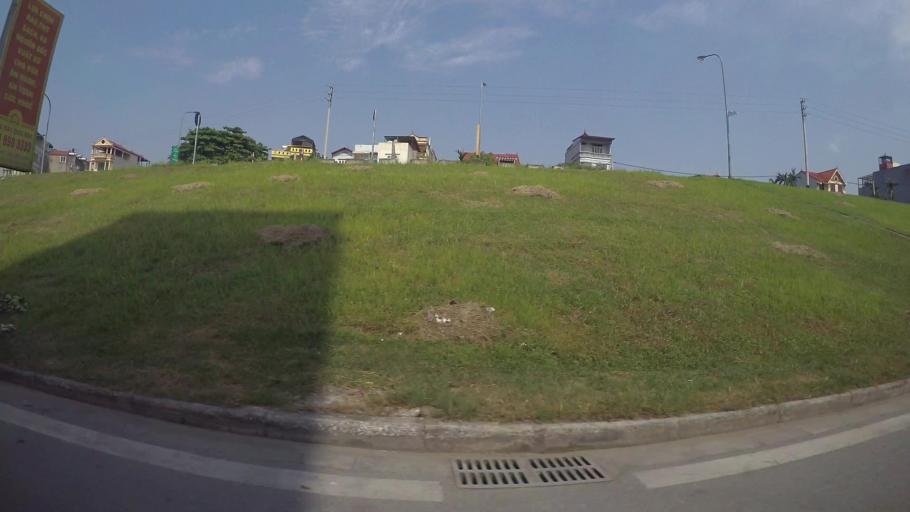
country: VN
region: Ha Noi
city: Hoan Kiem
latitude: 21.0529
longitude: 105.8643
